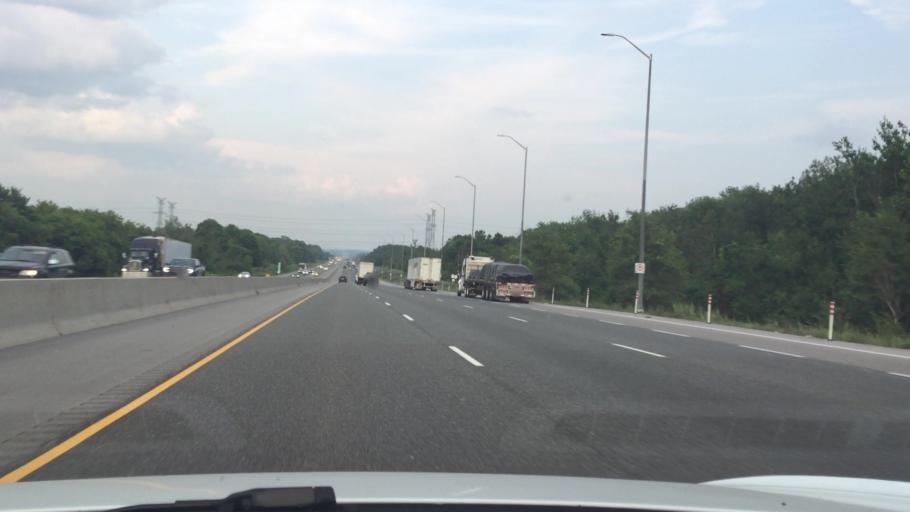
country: CA
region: Ontario
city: Cobourg
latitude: 43.9450
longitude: -78.4244
